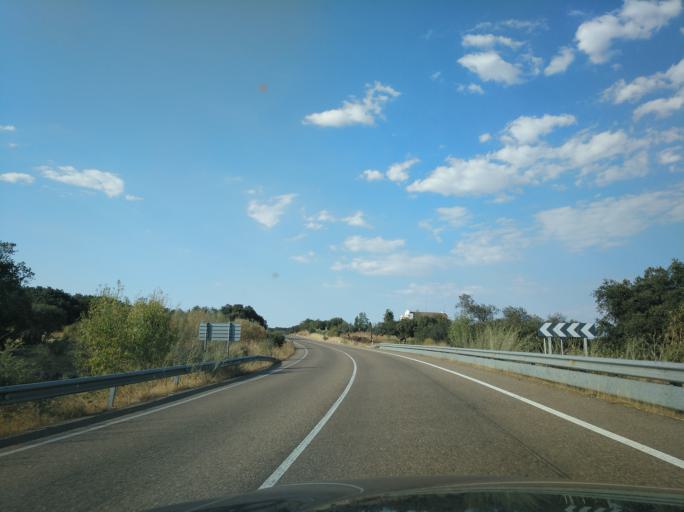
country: ES
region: Extremadura
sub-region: Provincia de Badajoz
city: Alconchel
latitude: 38.4740
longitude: -7.0676
